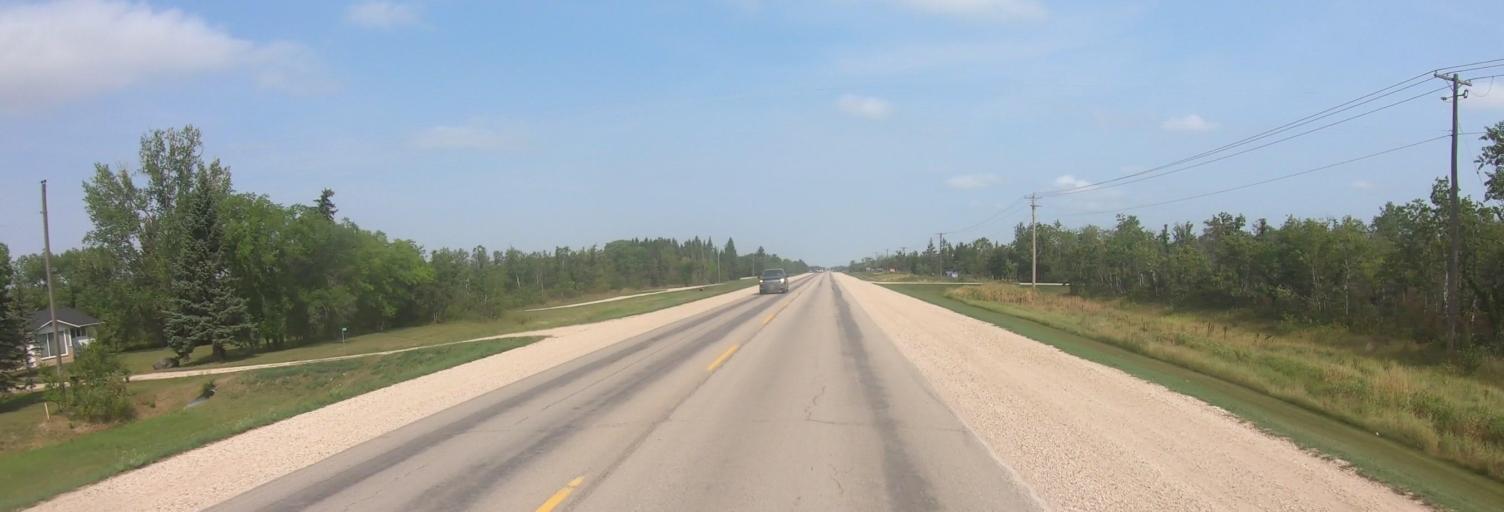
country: CA
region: Manitoba
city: Steinbach
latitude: 49.4896
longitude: -96.6912
